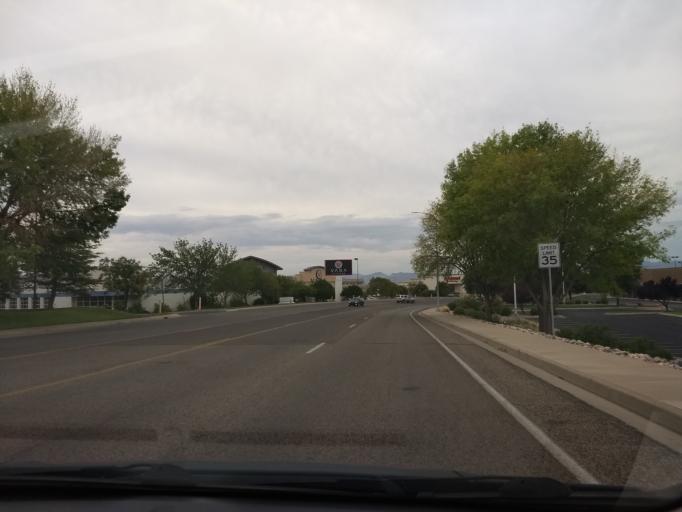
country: US
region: Utah
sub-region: Washington County
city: Washington
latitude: 37.1180
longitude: -113.5434
